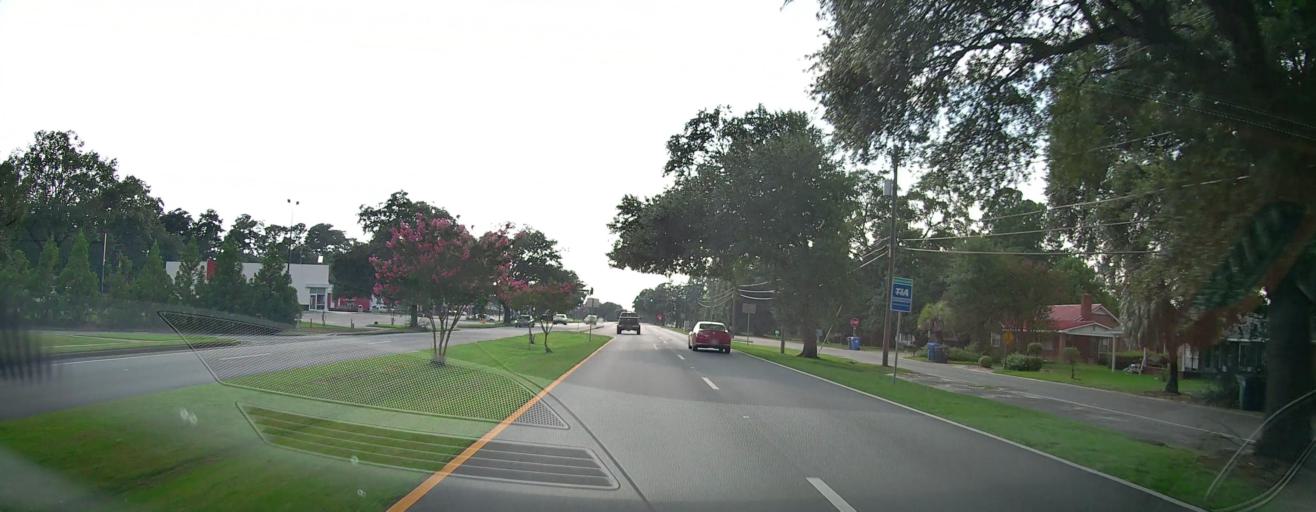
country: US
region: Georgia
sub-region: Laurens County
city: Dublin
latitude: 32.5360
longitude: -82.9288
